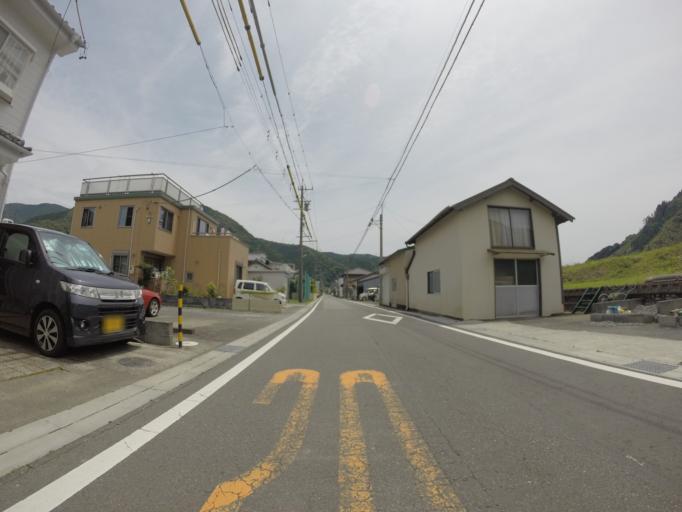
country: JP
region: Shizuoka
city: Shizuoka-shi
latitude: 35.0072
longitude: 138.2787
